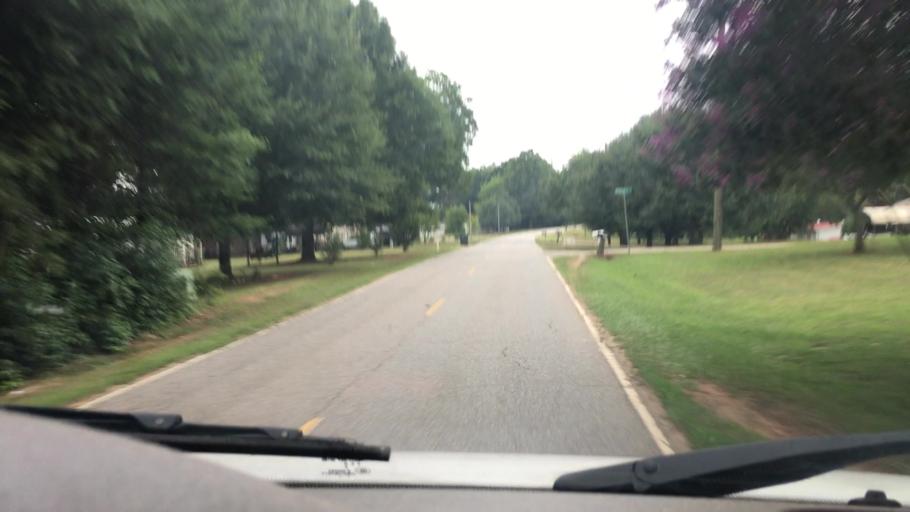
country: US
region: North Carolina
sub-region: Gaston County
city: Davidson
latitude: 35.5356
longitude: -80.8322
